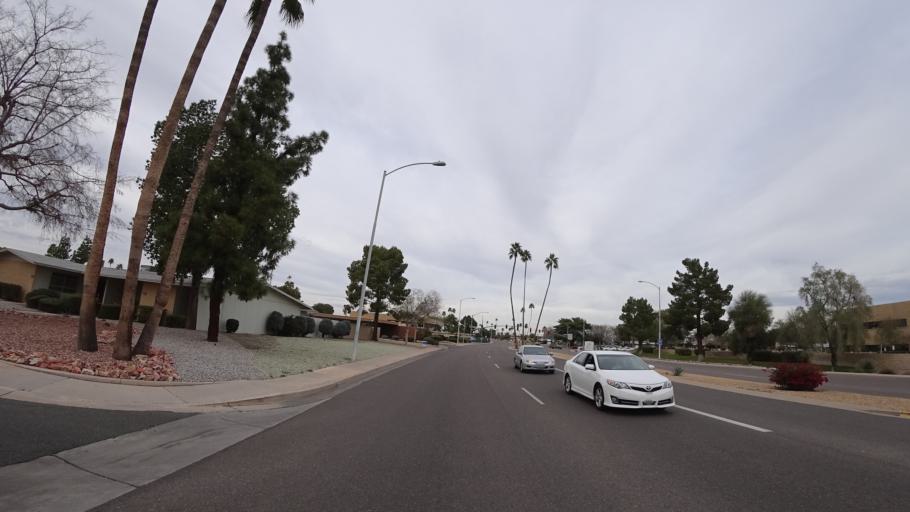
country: US
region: Arizona
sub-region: Maricopa County
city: Youngtown
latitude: 33.6044
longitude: -112.2900
